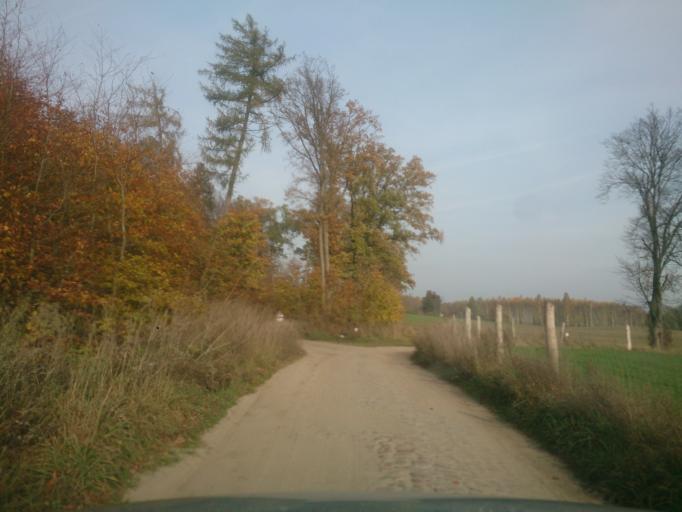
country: PL
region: Kujawsko-Pomorskie
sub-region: Powiat brodnicki
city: Brodnica
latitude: 53.3469
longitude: 19.3590
